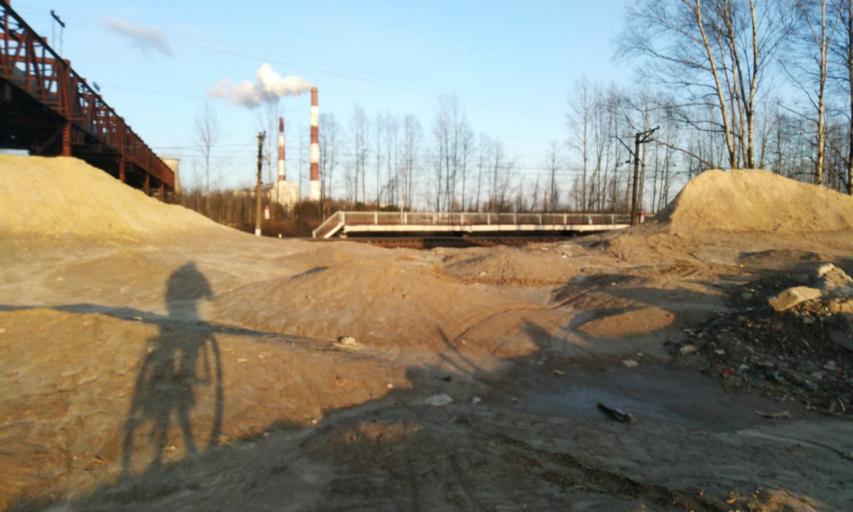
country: RU
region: Leningrad
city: Novoye Devyatkino
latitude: 60.0785
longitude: 30.4604
